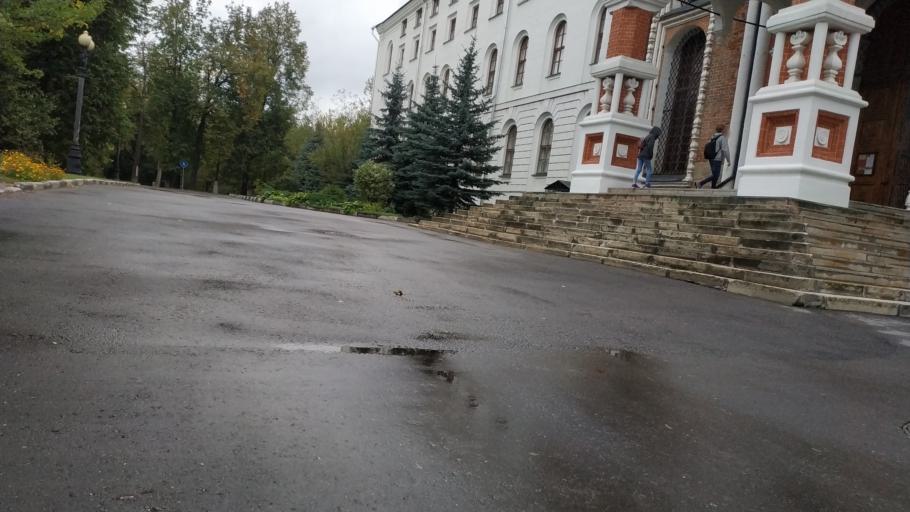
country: RU
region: Moscow
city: Metrogorodok
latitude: 55.7913
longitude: 37.7646
